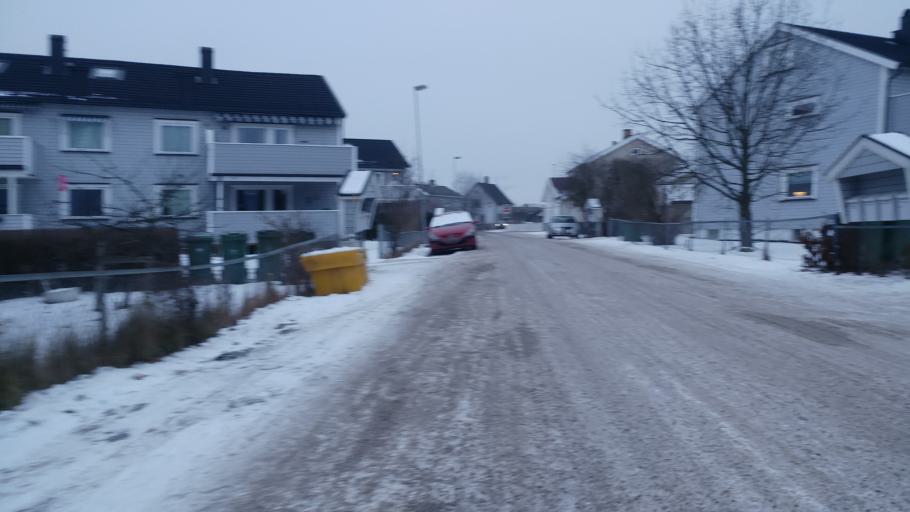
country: NO
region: Akershus
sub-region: Skedsmo
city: Lillestrom
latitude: 59.9631
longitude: 11.0339
